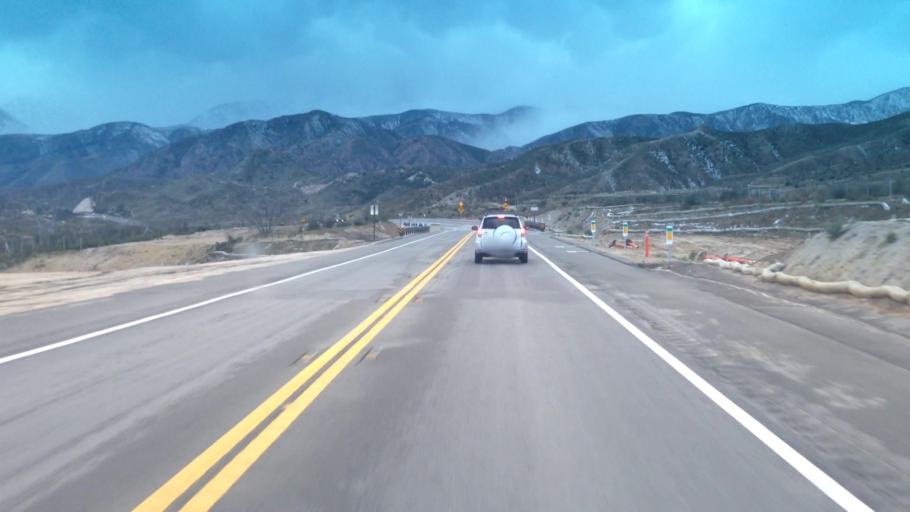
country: US
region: California
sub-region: San Bernardino County
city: Oak Hills
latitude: 34.3263
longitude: -117.4526
